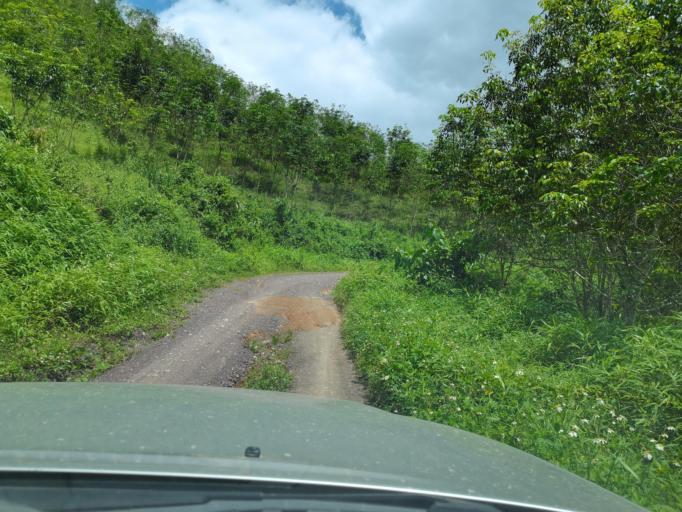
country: LA
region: Loungnamtha
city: Muang Long
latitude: 20.7188
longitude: 101.0140
